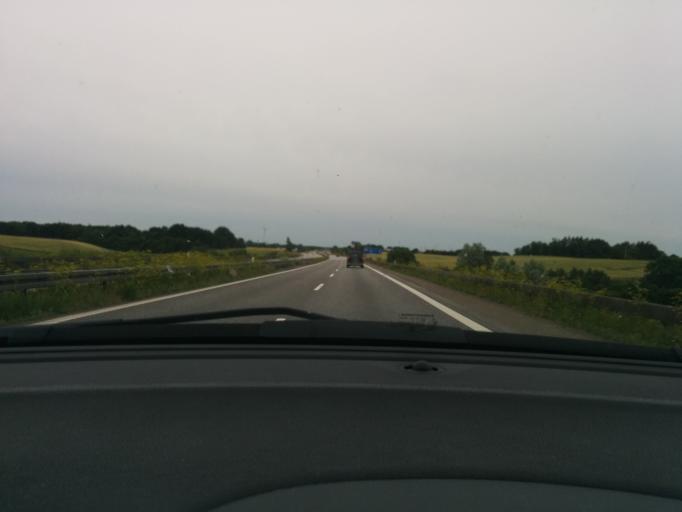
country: DK
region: Zealand
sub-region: Faxe Kommune
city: Ronnede
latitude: 55.1748
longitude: 11.9588
